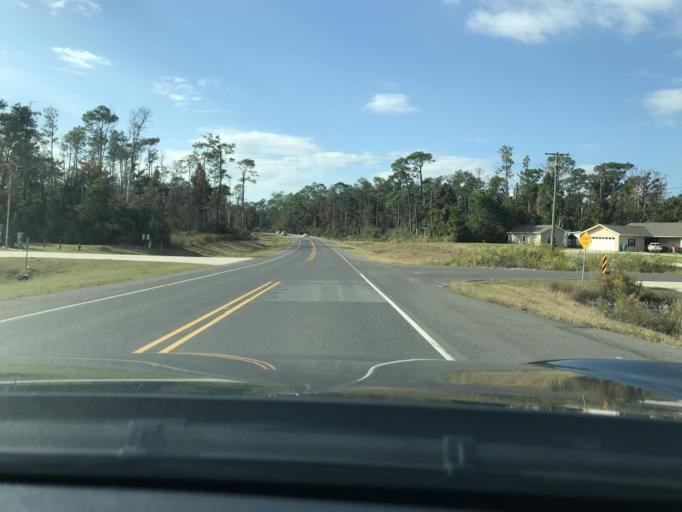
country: US
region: Louisiana
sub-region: Calcasieu Parish
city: Moss Bluff
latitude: 30.3040
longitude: -93.2491
